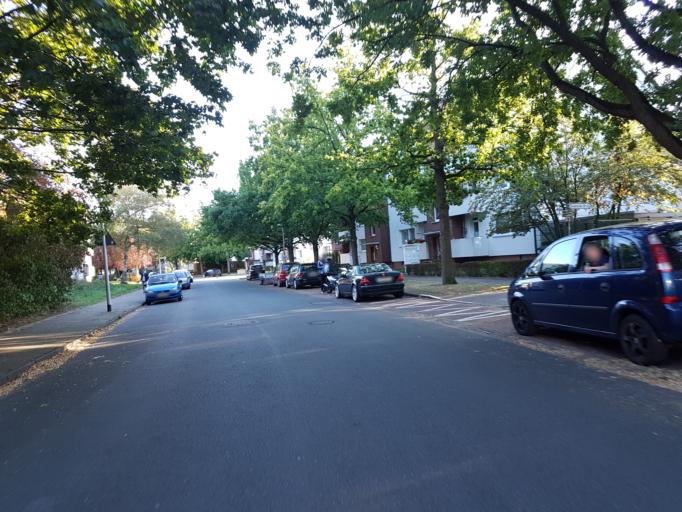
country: DE
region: Lower Saxony
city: Hannover
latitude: 52.4055
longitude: 9.7412
